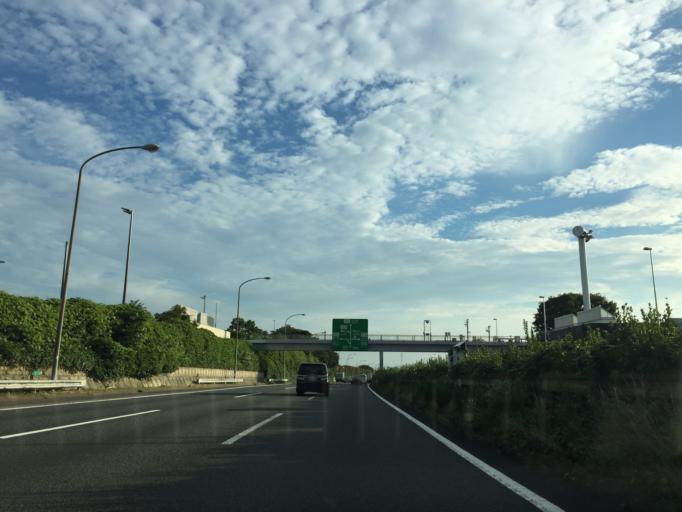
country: JP
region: Kanagawa
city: Atsugi
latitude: 35.4322
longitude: 139.4008
